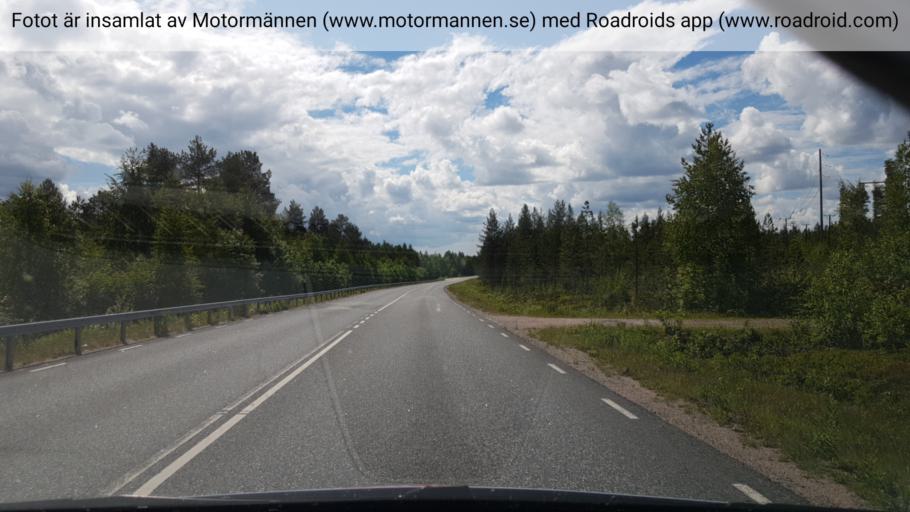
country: SE
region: Norrbotten
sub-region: Overtornea Kommun
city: OEvertornea
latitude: 66.3461
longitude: 23.6486
